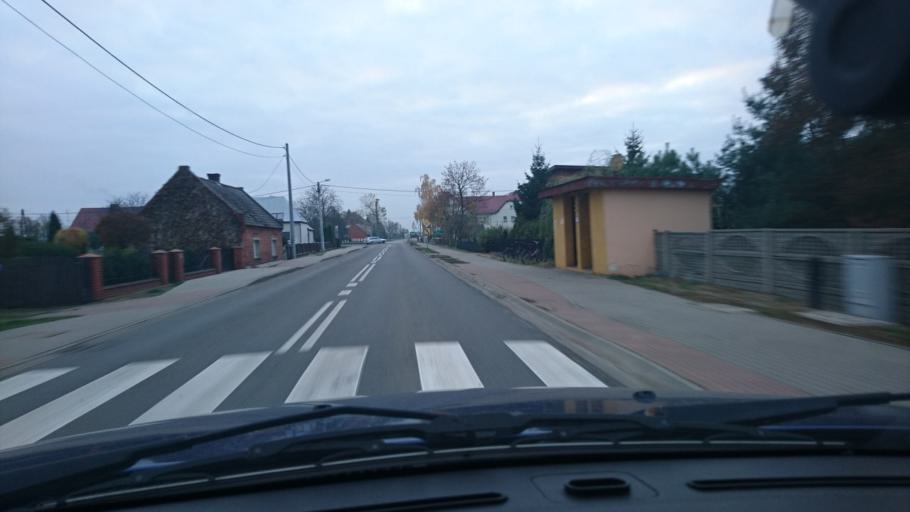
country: PL
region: Greater Poland Voivodeship
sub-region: Powiat ostrowski
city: Odolanow
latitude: 51.5420
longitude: 17.6531
